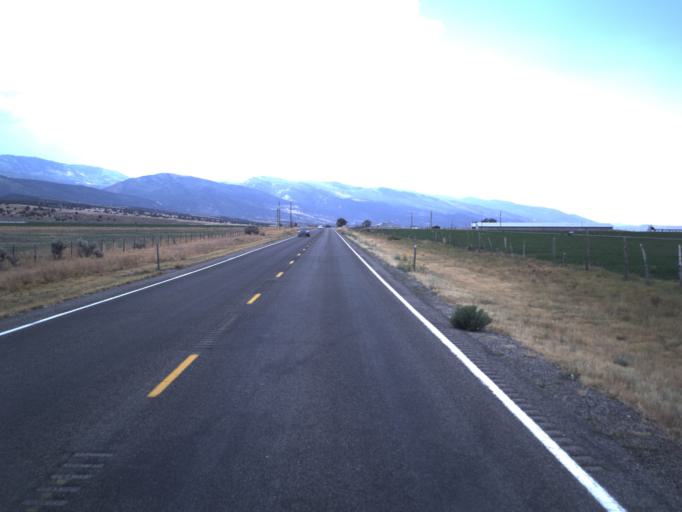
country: US
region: Utah
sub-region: Sanpete County
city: Ephraim
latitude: 39.4359
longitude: -111.5624
